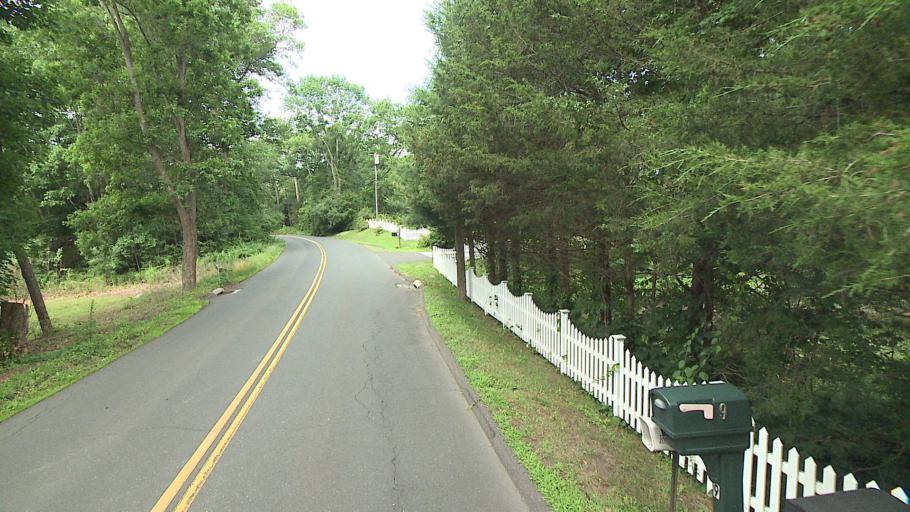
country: US
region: Connecticut
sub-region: New Haven County
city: Southbury
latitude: 41.4296
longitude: -73.1908
